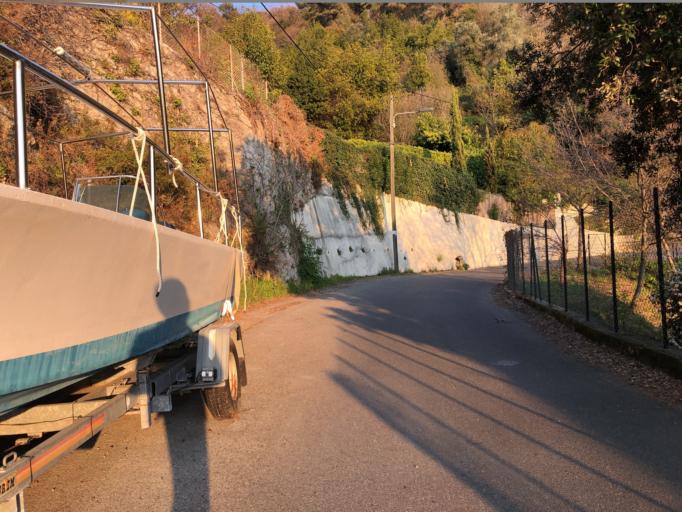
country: FR
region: Provence-Alpes-Cote d'Azur
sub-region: Departement des Alpes-Maritimes
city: Villefranche-sur-Mer
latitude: 43.7182
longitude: 7.2994
